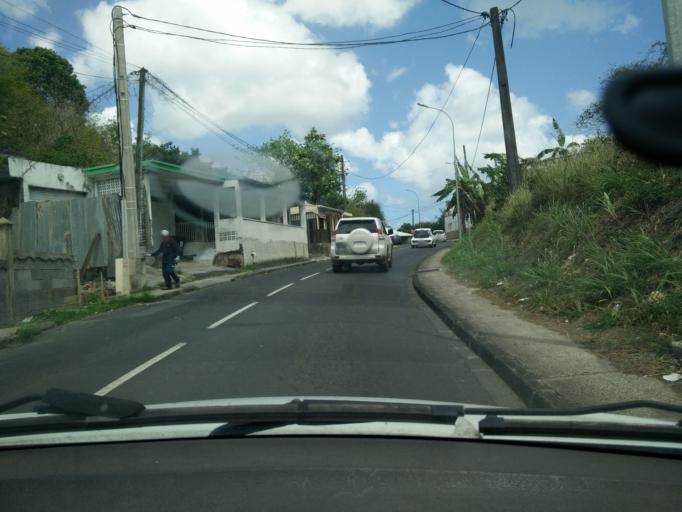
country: GP
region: Guadeloupe
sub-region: Guadeloupe
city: Les Abymes
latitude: 16.2620
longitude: -61.5017
